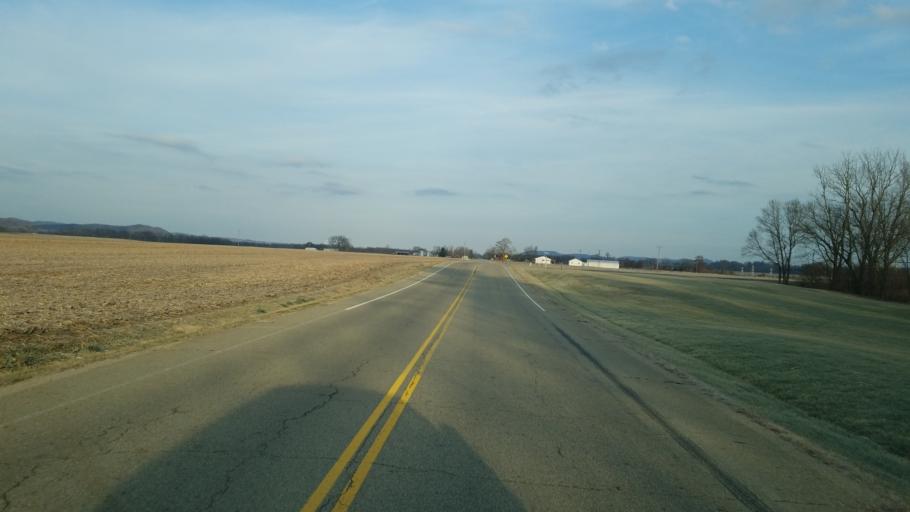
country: US
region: Ohio
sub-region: Ross County
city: Chillicothe
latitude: 39.2491
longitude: -82.8716
